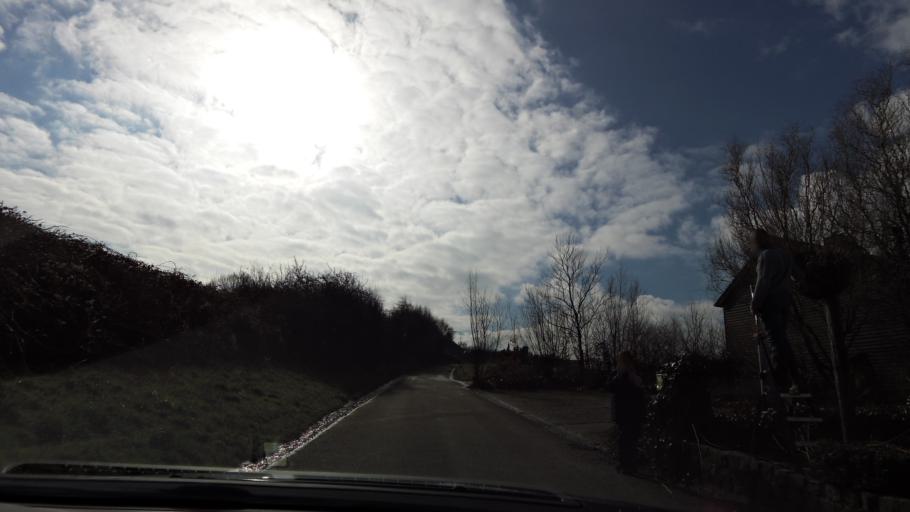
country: BE
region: Wallonia
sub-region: Province de Liege
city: Plombieres
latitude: 50.7823
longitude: 5.9267
